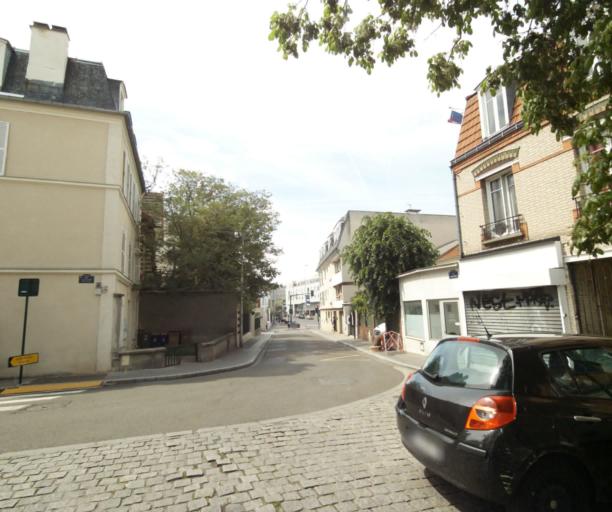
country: FR
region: Ile-de-France
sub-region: Departement des Hauts-de-Seine
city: Colombes
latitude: 48.9229
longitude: 2.2591
